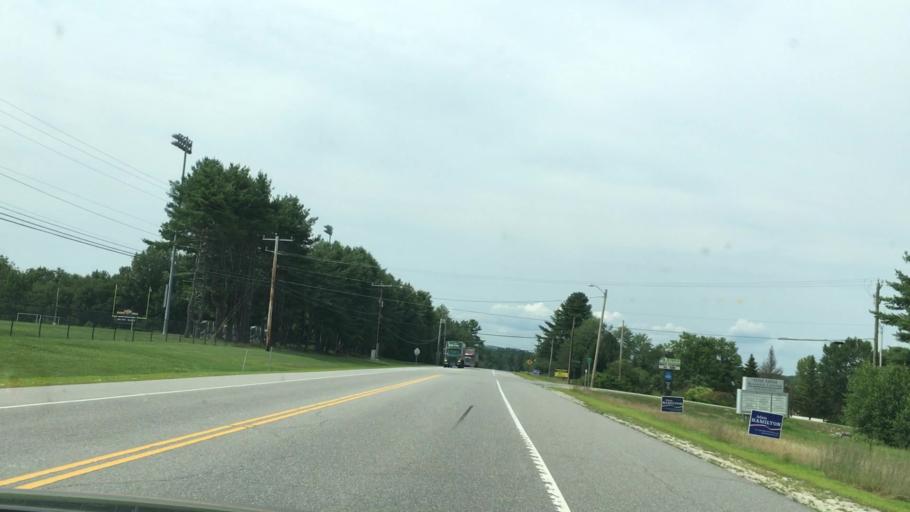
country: US
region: New Hampshire
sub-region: Hillsborough County
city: Peterborough
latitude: 42.9127
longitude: -71.9387
